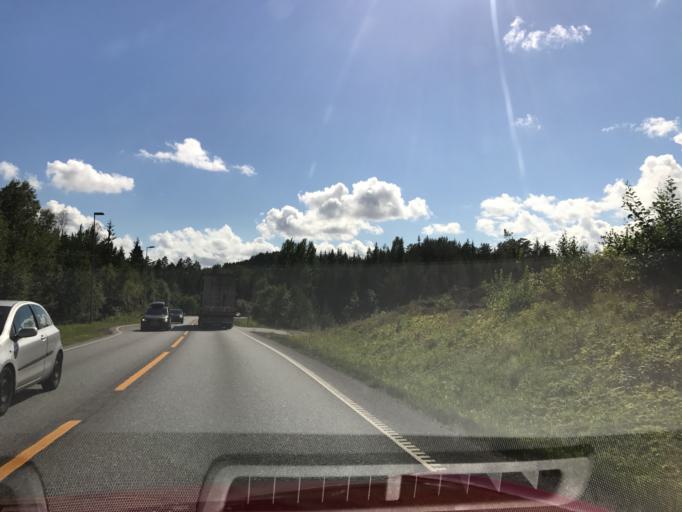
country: NO
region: Telemark
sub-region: Kragero
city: Kragero
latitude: 58.9689
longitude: 9.4925
